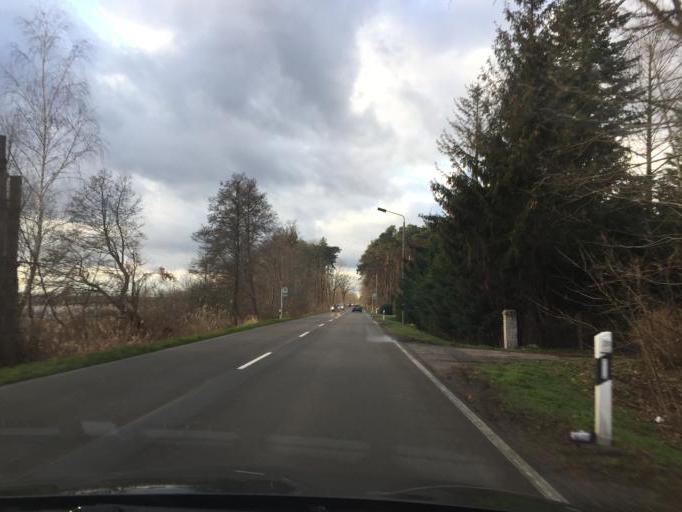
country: DE
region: Brandenburg
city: Kolkwitz
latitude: 51.7504
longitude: 14.2300
